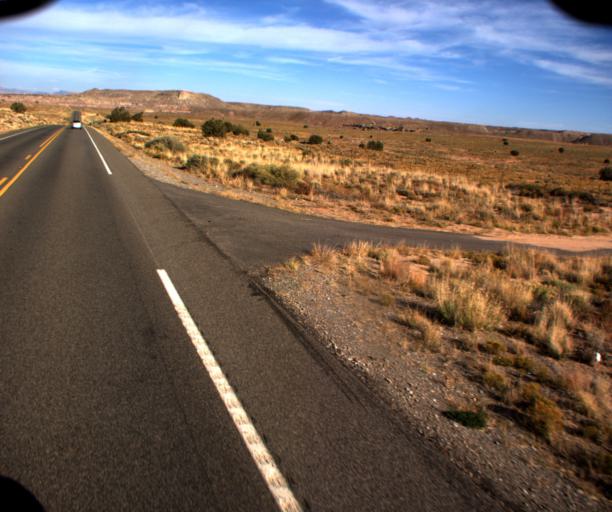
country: US
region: New Mexico
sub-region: San Juan County
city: Shiprock
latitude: 36.9320
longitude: -109.1443
